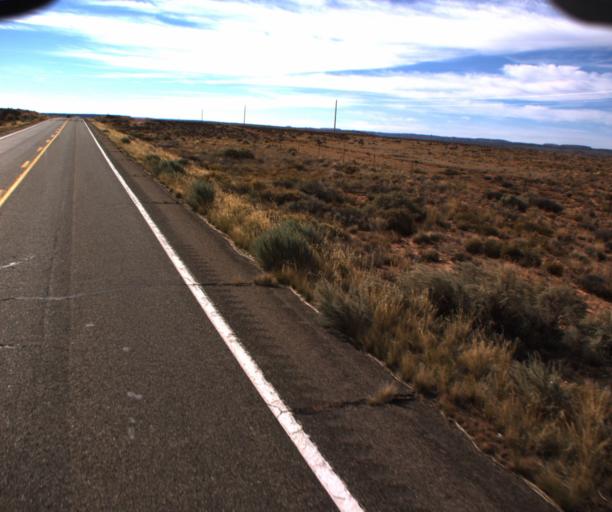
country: US
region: Arizona
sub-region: Coconino County
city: LeChee
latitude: 36.7271
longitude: -111.2807
